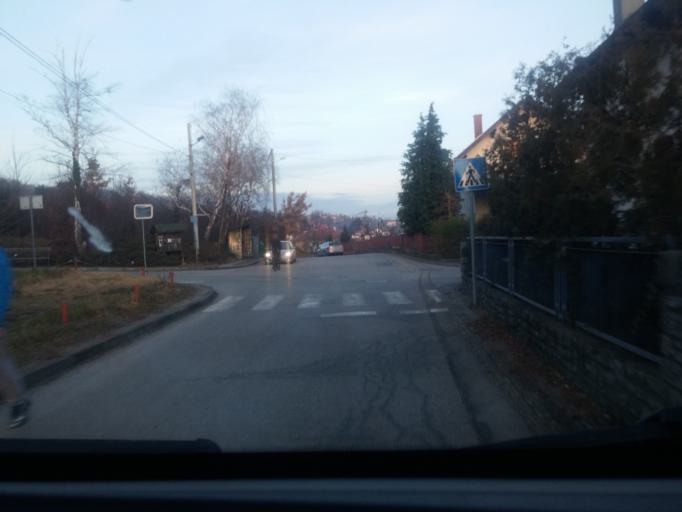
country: HR
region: Grad Zagreb
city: Stenjevec
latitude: 45.8321
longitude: 15.8803
